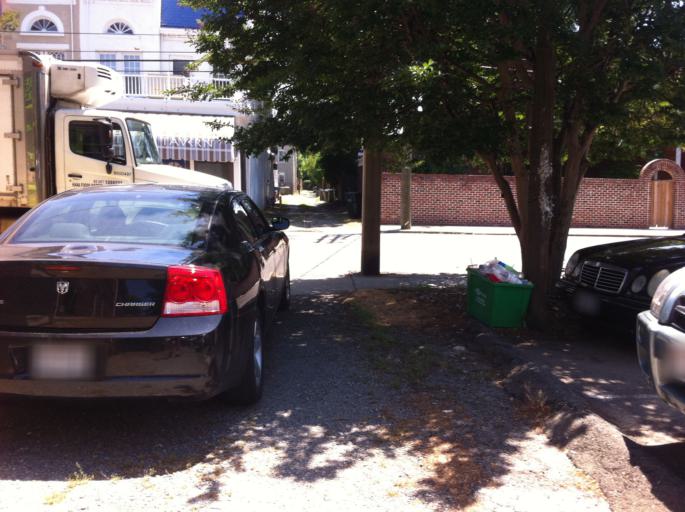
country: US
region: Virginia
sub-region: City of Richmond
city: Richmond
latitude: 37.5568
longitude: -77.4707
